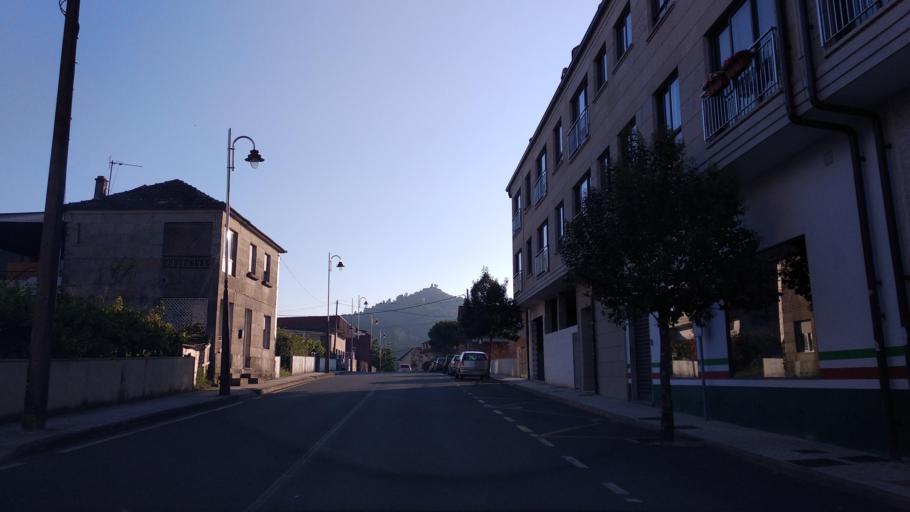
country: ES
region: Galicia
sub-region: Provincia de Pontevedra
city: Redondela
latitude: 42.3384
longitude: -8.5700
